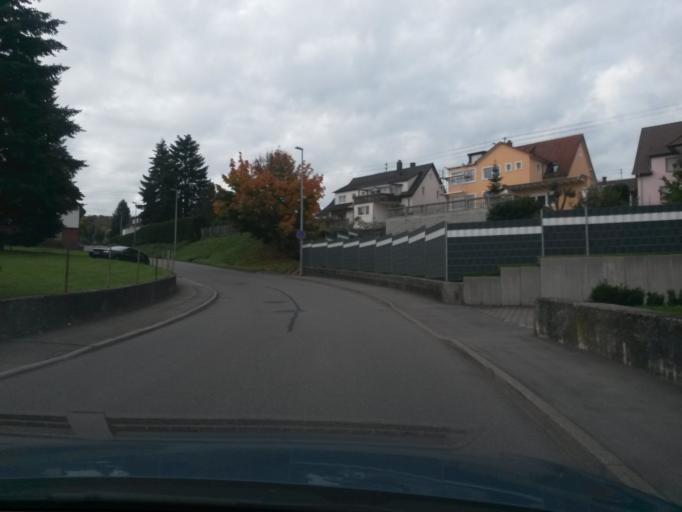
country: DE
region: Baden-Wuerttemberg
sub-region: Karlsruhe Region
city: Neuenburg
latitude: 48.8687
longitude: 8.5829
